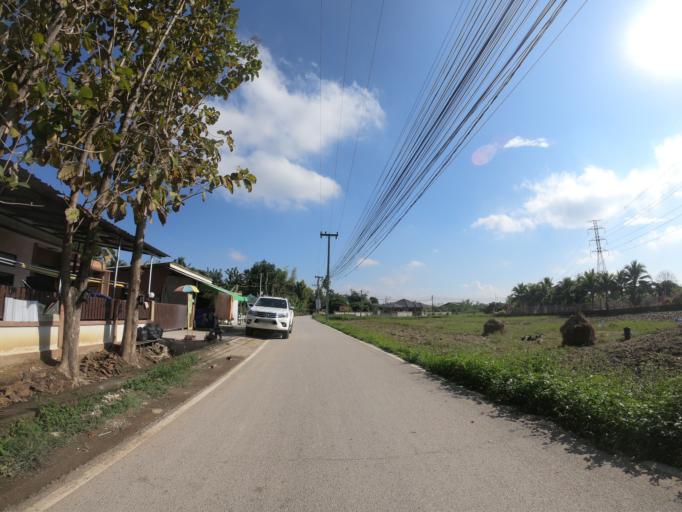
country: TH
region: Chiang Mai
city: Saraphi
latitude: 18.7132
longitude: 99.0175
